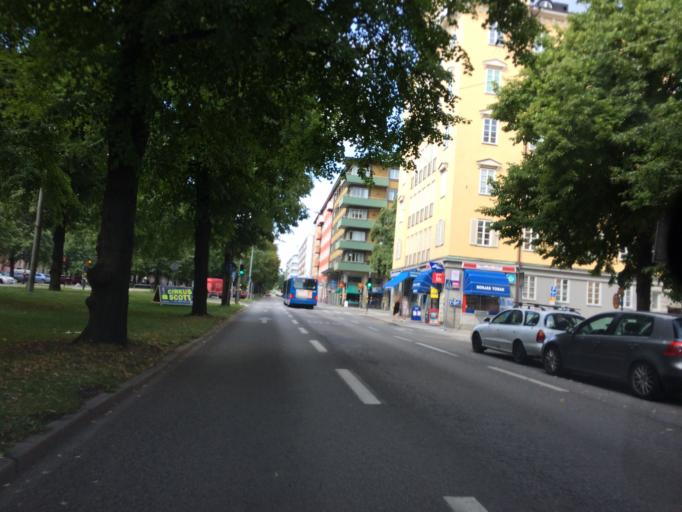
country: SE
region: Stockholm
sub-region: Stockholms Kommun
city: OEstermalm
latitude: 59.3407
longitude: 18.0917
